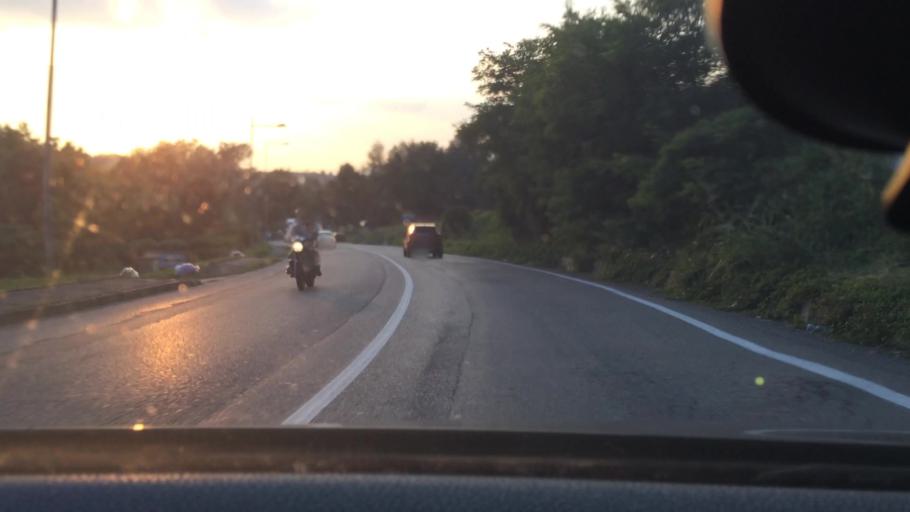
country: IT
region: Lombardy
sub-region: Provincia di Lecco
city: Nibionno
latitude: 45.7497
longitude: 9.2599
